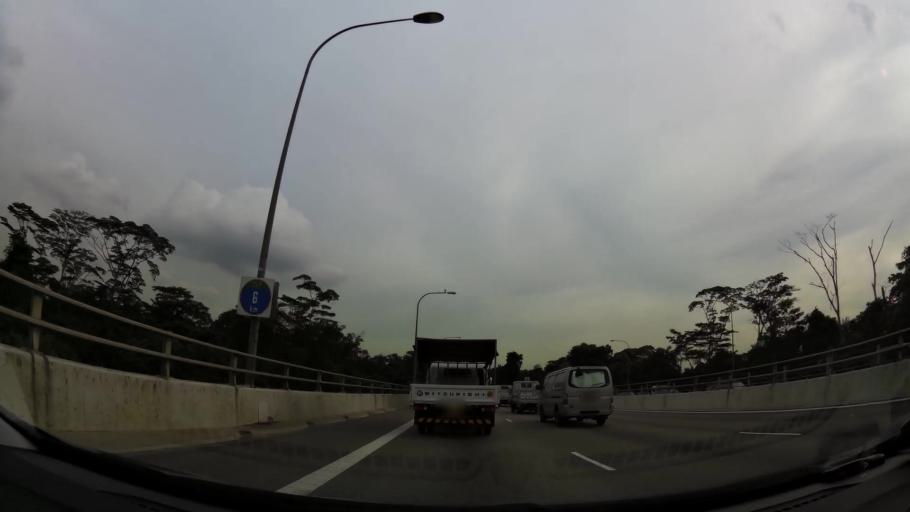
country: MY
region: Johor
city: Johor Bahru
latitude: 1.3992
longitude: 103.8136
